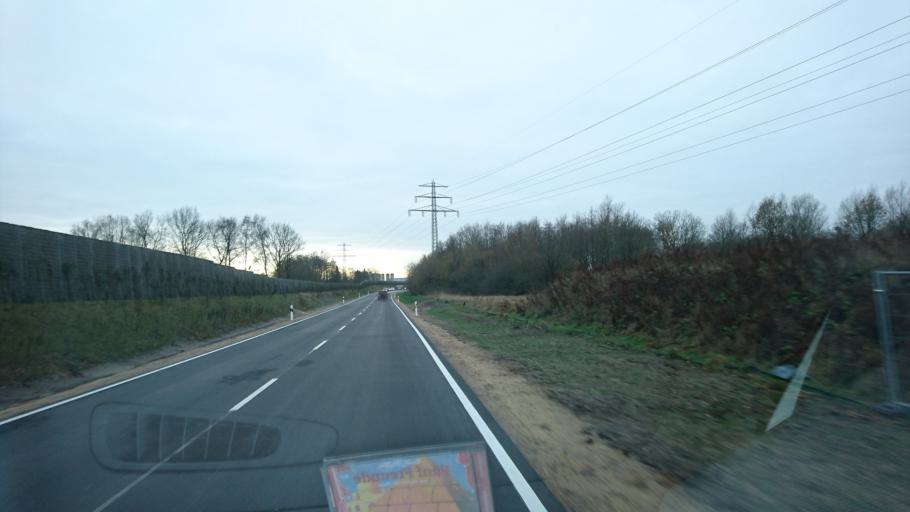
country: DE
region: Schleswig-Holstein
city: Kummerfeld
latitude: 53.6742
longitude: 9.7832
